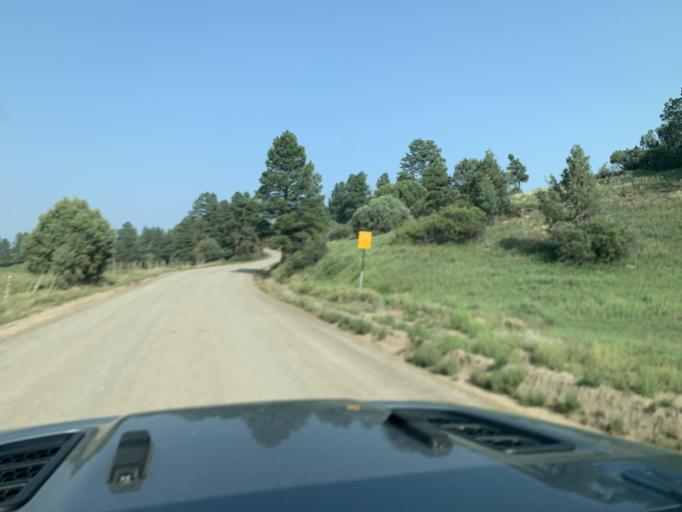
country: US
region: Colorado
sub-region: Archuleta County
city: Pagosa Springs
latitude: 37.2236
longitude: -107.2156
